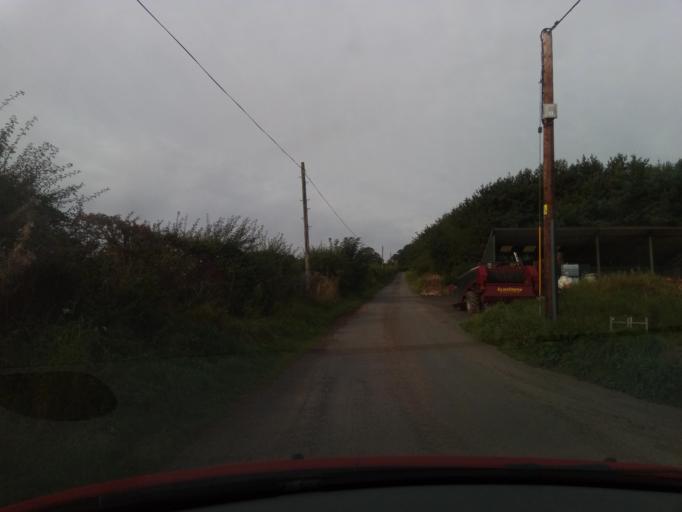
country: GB
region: Scotland
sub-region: The Scottish Borders
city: Jedburgh
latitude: 55.4807
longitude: -2.4912
